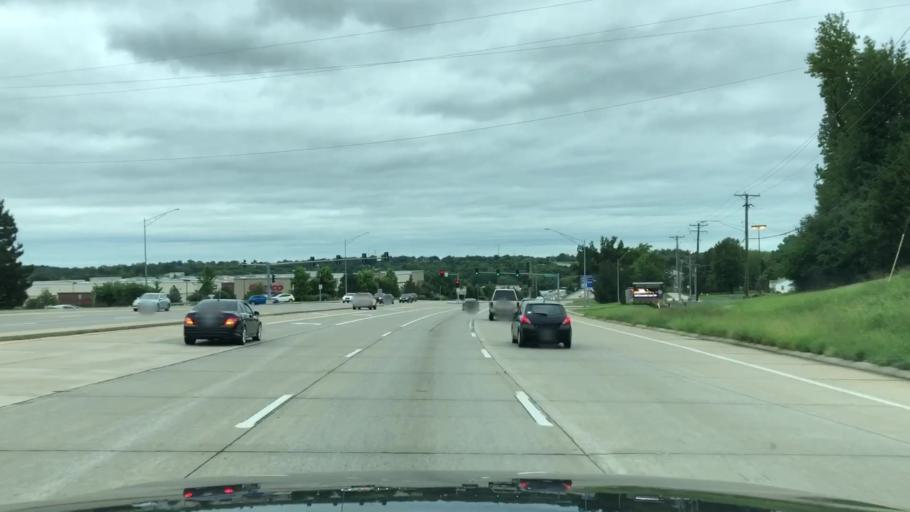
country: US
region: Missouri
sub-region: Saint Louis County
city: Manchester
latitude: 38.6002
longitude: -90.5091
